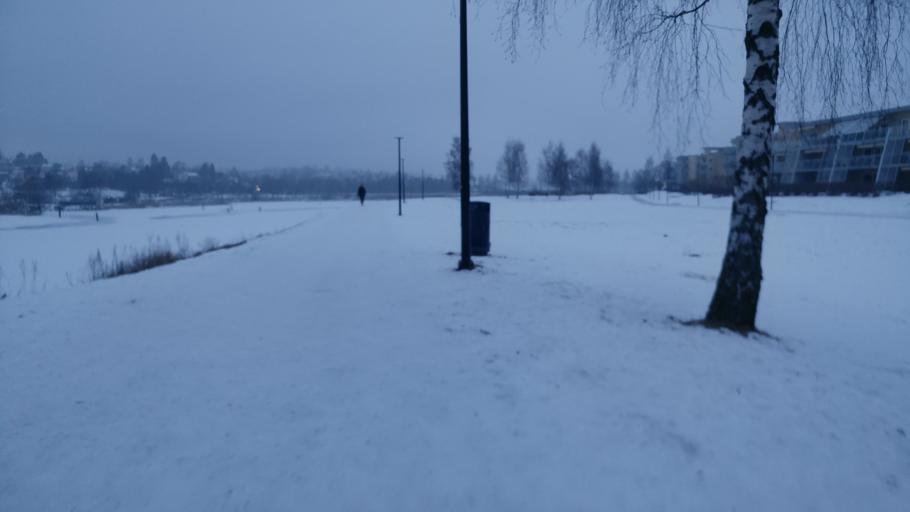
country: NO
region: Akershus
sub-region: Skedsmo
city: Lillestrom
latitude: 59.9544
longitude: 11.0337
